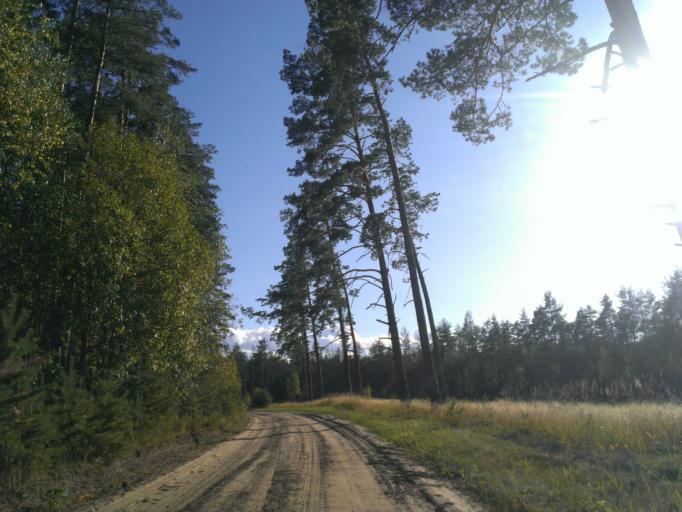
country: LV
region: Adazi
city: Adazi
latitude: 57.0512
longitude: 24.2526
